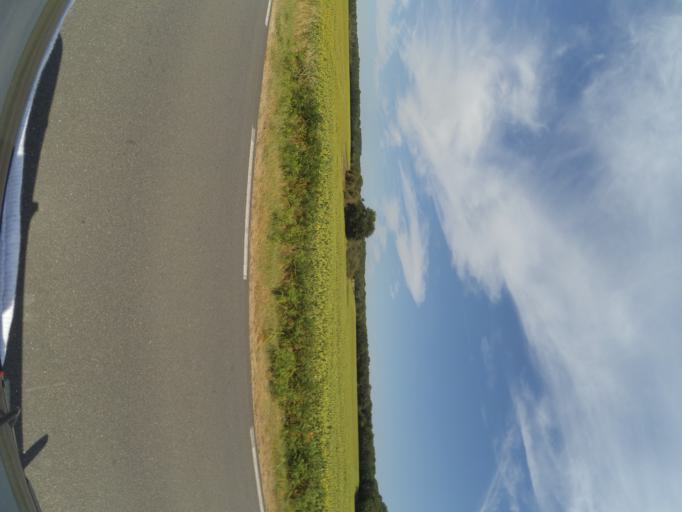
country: FR
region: Poitou-Charentes
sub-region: Departement de la Charente
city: Confolens
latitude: 46.0548
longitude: 0.6124
